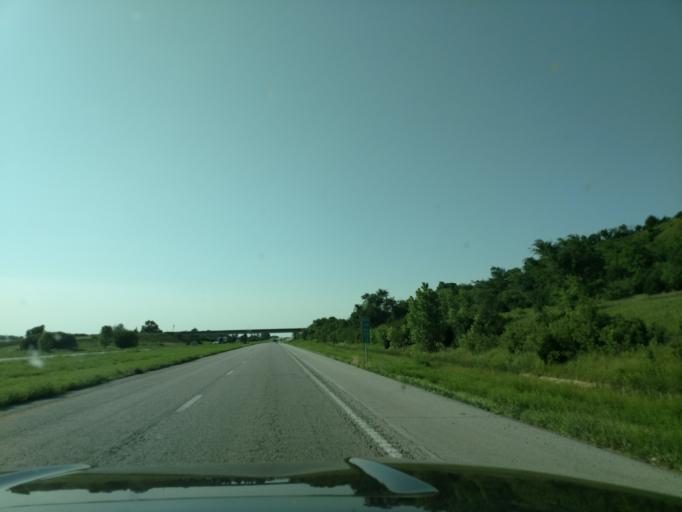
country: US
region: Iowa
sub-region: Fremont County
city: Hamburg
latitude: 40.5570
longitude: -95.6328
